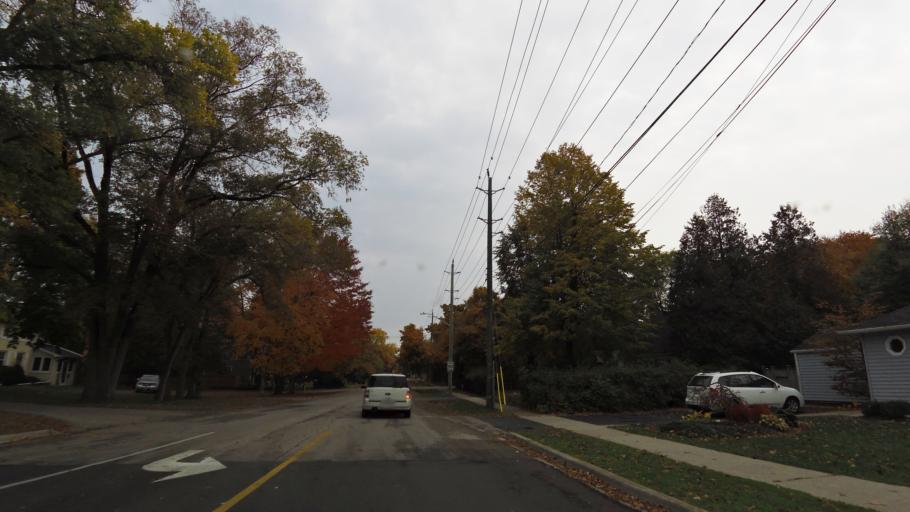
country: CA
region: Ontario
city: Oakville
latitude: 43.4340
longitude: -79.6850
